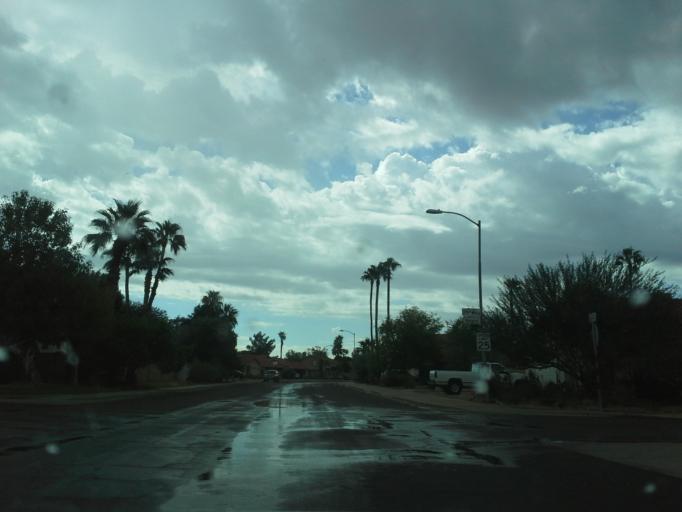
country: US
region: Arizona
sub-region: Maricopa County
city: Paradise Valley
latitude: 33.6156
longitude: -112.0399
